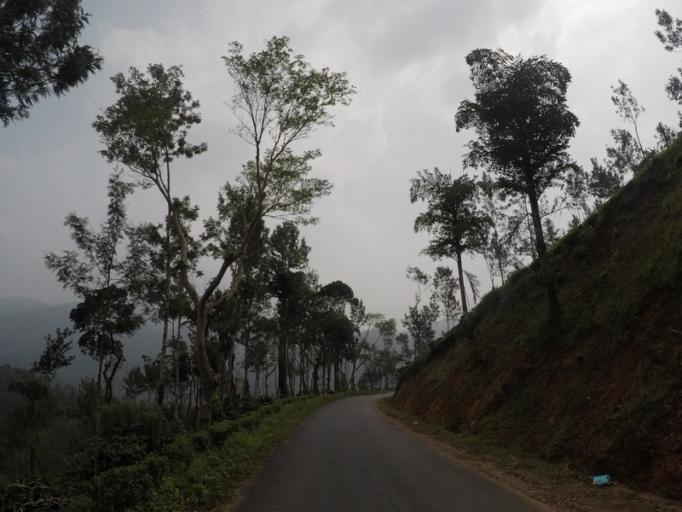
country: IN
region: Karnataka
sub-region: Chikmagalur
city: Mudigere
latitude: 13.1671
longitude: 75.4408
